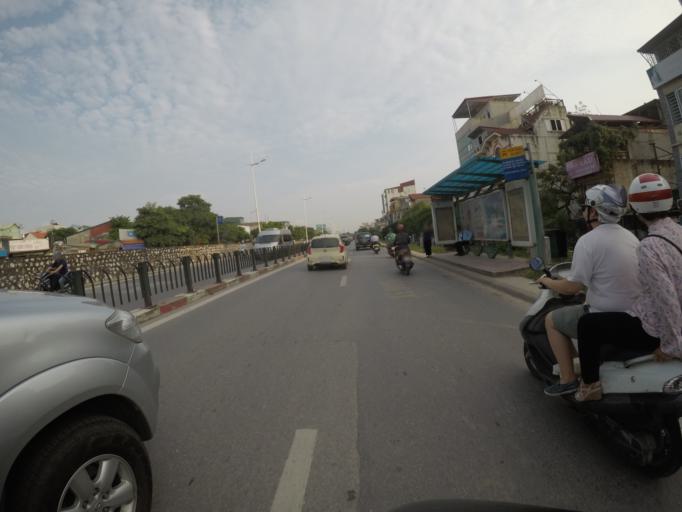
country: VN
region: Ha Noi
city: Tay Ho
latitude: 21.0805
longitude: 105.8185
